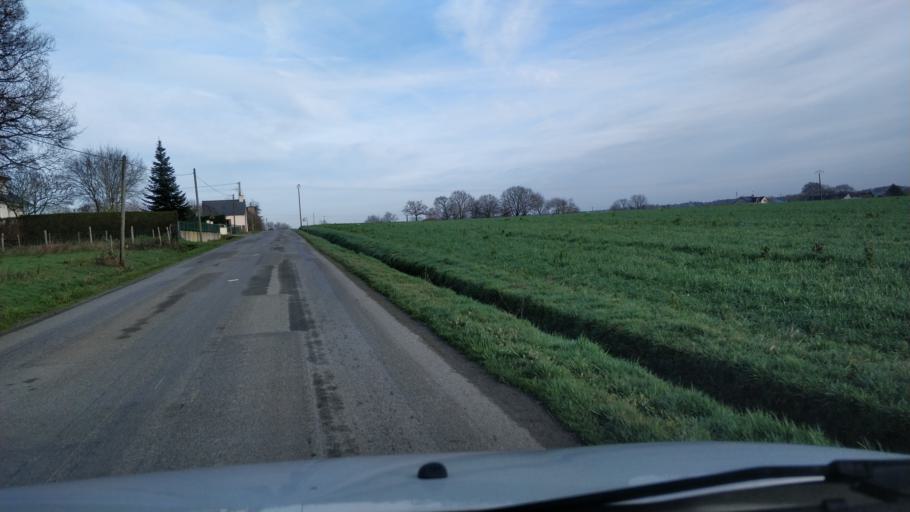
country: FR
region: Brittany
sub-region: Departement d'Ille-et-Vilaine
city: Argentre-du-Plessis
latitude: 48.0338
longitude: -1.1669
